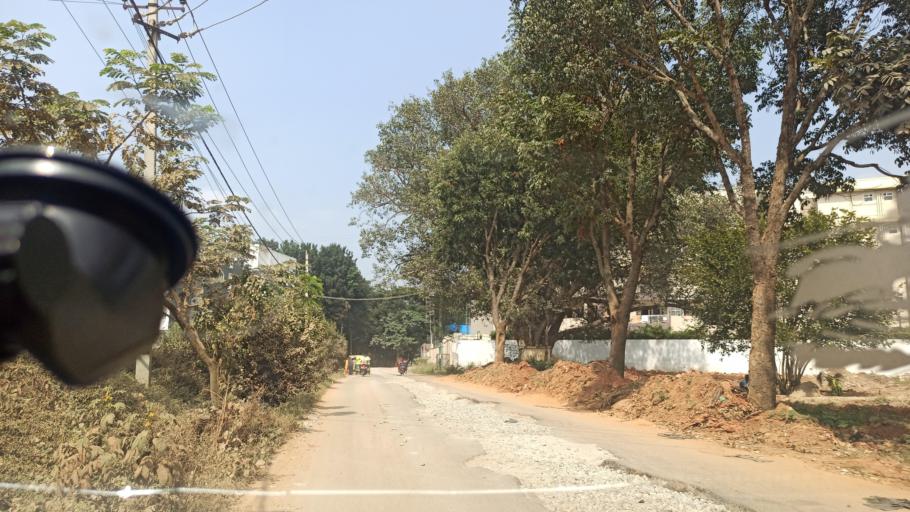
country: IN
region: Karnataka
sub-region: Bangalore Urban
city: Yelahanka
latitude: 13.0922
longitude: 77.6194
